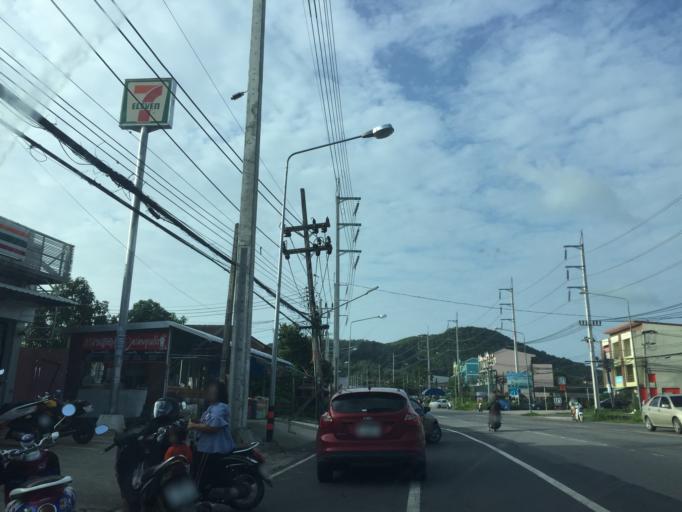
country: TH
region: Phuket
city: Mueang Phuket
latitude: 7.8482
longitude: 98.3822
